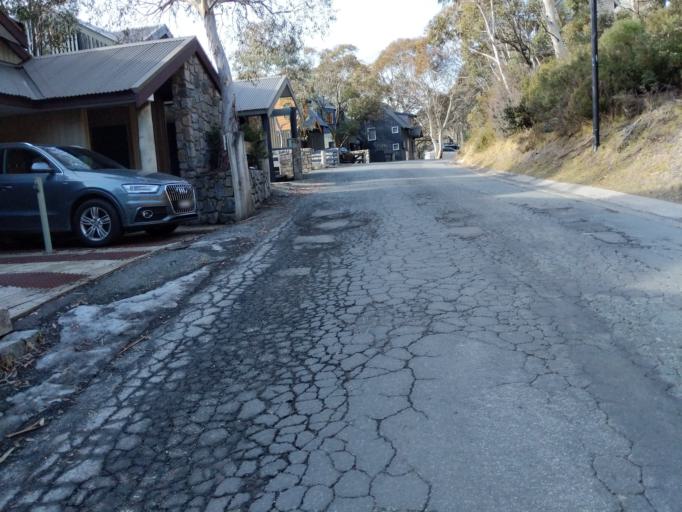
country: AU
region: New South Wales
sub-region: Snowy River
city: Jindabyne
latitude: -36.5067
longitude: 148.3025
